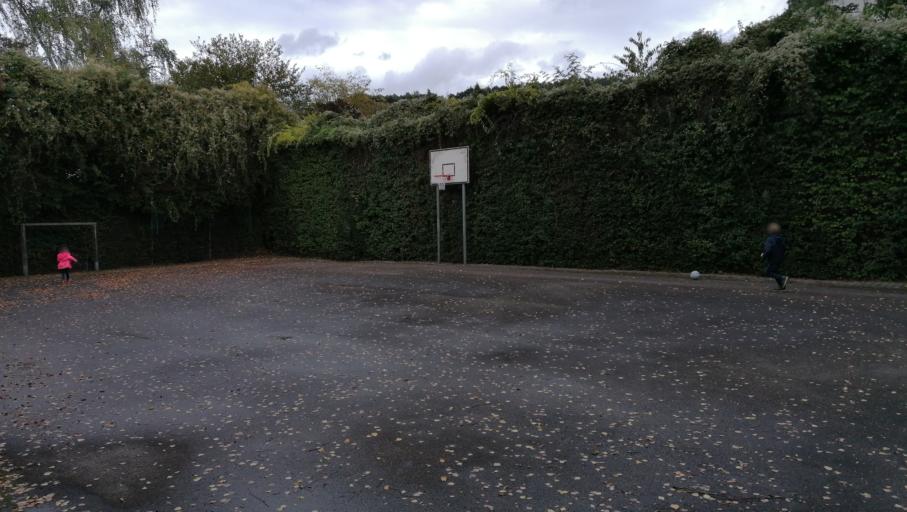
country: DE
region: Baden-Wuerttemberg
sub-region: Regierungsbezirk Stuttgart
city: Weinstadt-Endersbach
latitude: 48.8240
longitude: 9.3804
